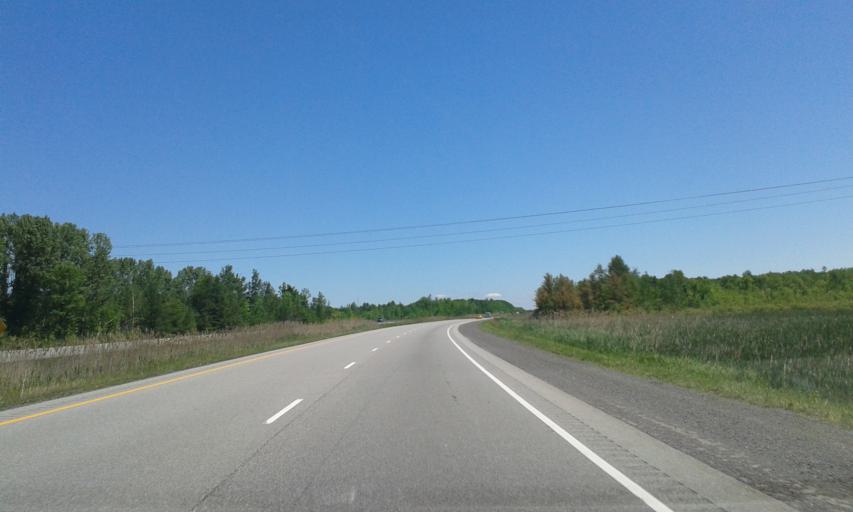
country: CA
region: Ontario
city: Prescott
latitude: 44.7781
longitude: -75.4566
